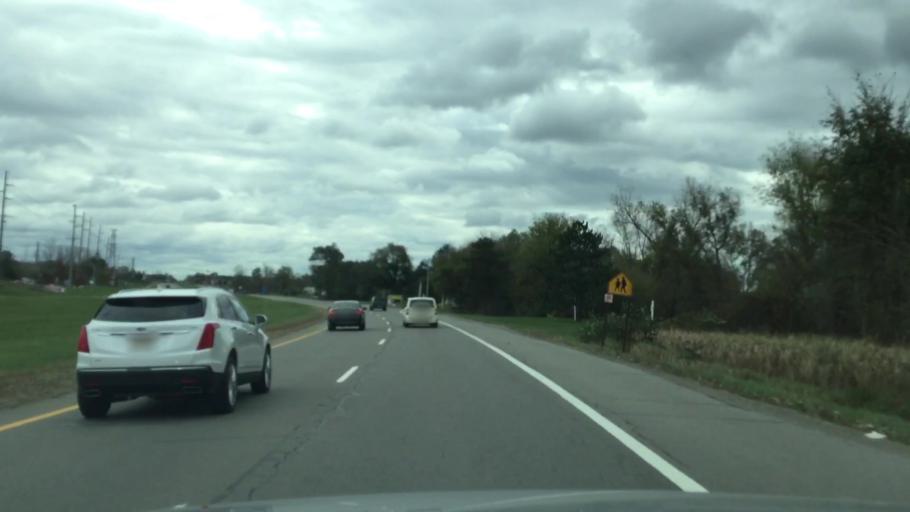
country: US
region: Michigan
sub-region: Oakland County
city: Milford
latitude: 42.6487
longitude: -83.5394
